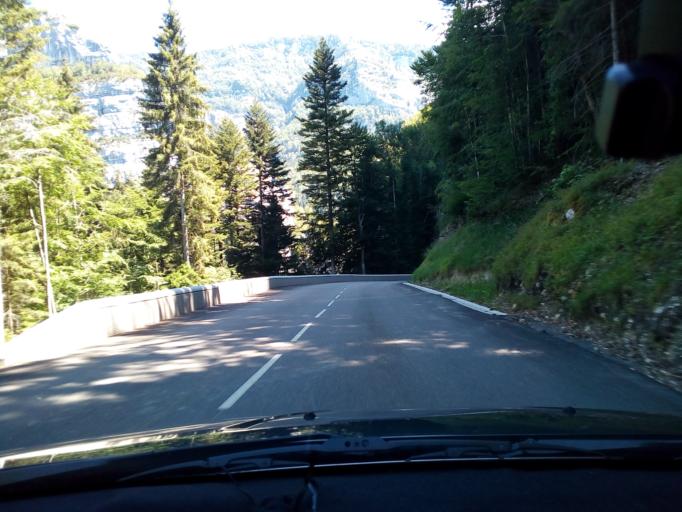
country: FR
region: Rhone-Alpes
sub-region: Departement de l'Isere
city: Meaudre
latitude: 45.0828
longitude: 5.4757
